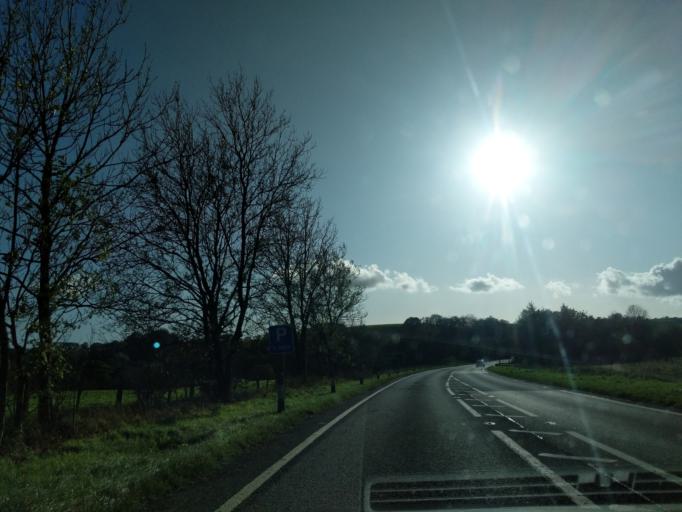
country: GB
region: Scotland
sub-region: Dumfries and Galloway
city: Castle Douglas
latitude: 54.9794
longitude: -3.8853
